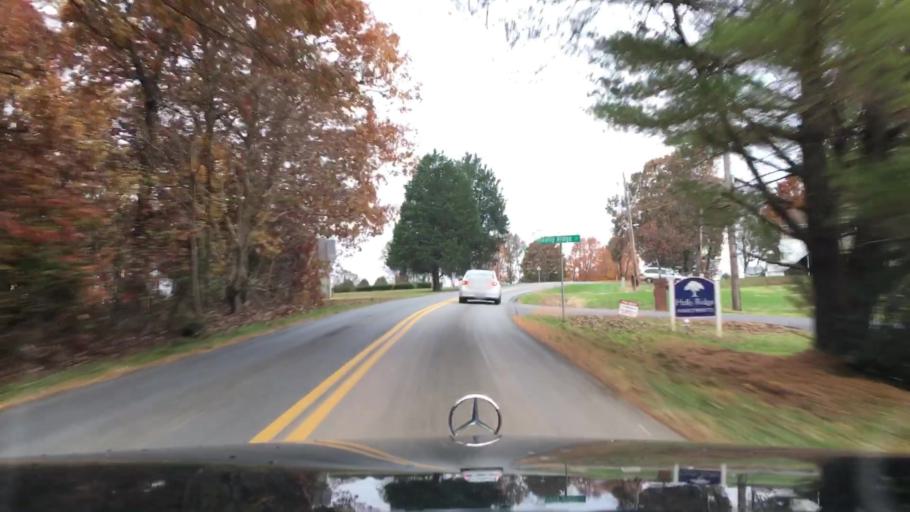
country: US
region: Virginia
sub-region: Campbell County
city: Timberlake
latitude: 37.2955
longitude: -79.2813
